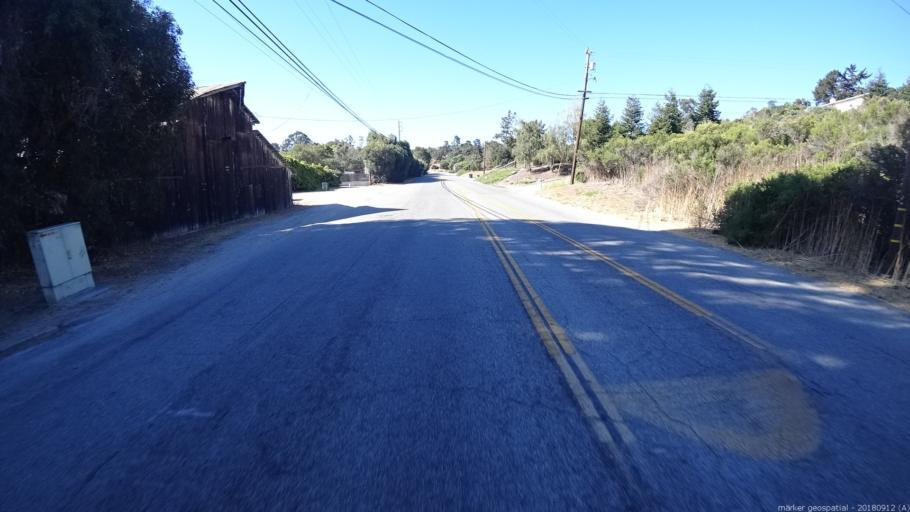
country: US
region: California
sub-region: Monterey County
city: Carmel Valley Village
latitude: 36.5747
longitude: -121.7293
